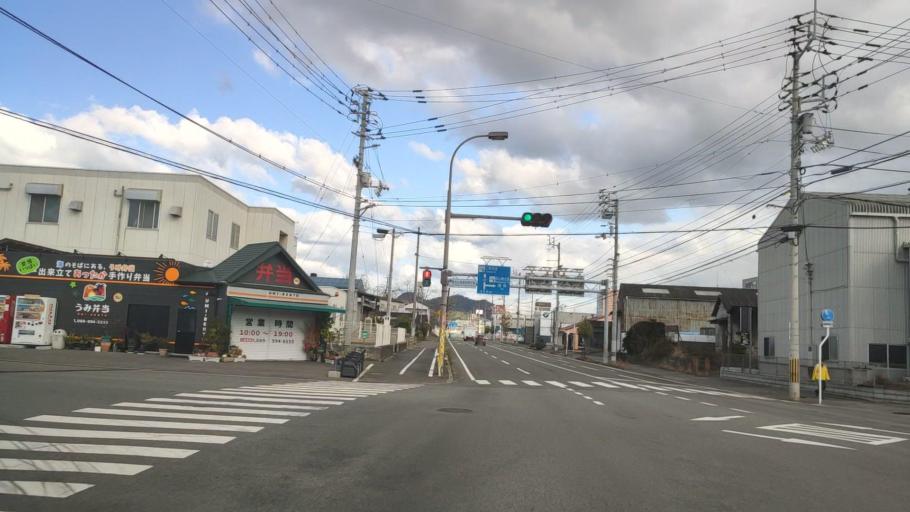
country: JP
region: Ehime
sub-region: Shikoku-chuo Shi
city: Matsuyama
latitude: 33.8534
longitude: 132.7130
